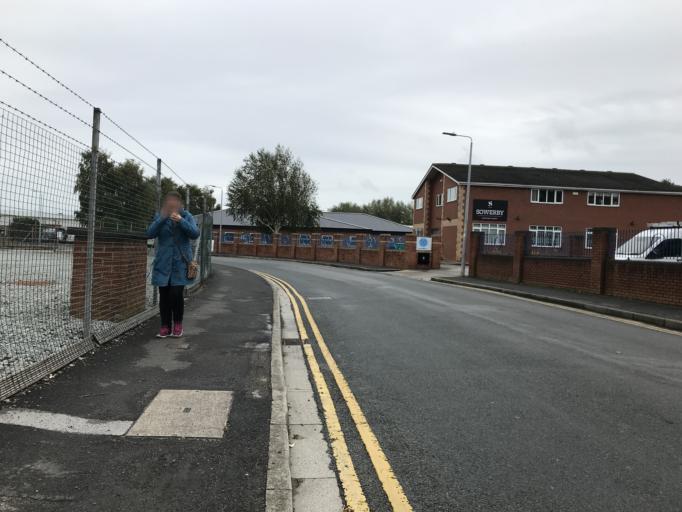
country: GB
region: England
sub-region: East Riding of Yorkshire
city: Beverley
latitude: 53.8402
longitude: -0.4006
